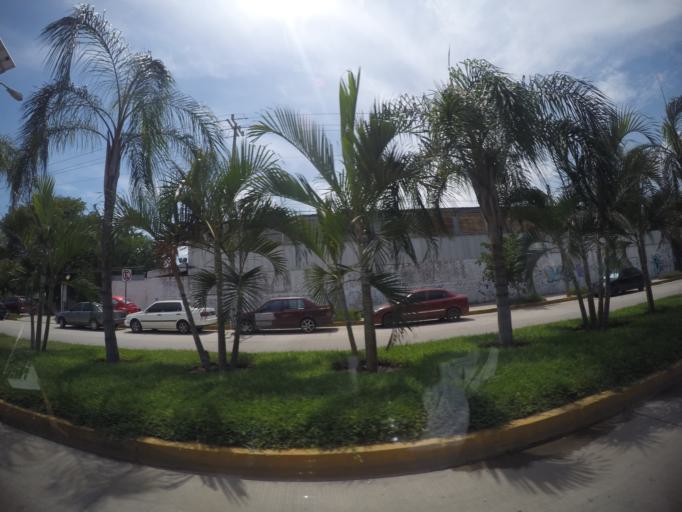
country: MX
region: Guerrero
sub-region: Acapulco de Juarez
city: Nueva Frontera
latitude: 16.9031
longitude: -99.8277
